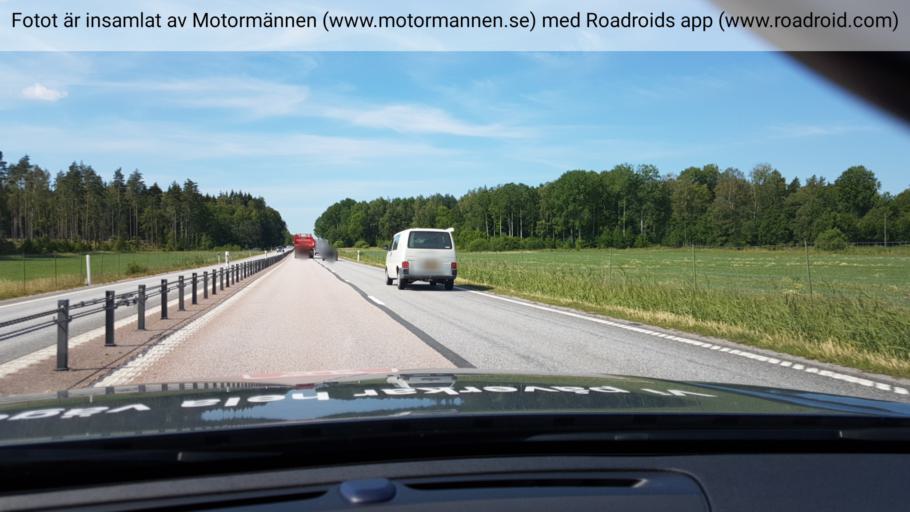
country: SE
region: Vaestmanland
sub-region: Kungsors Kommun
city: Kungsoer
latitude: 59.4169
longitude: 16.1539
